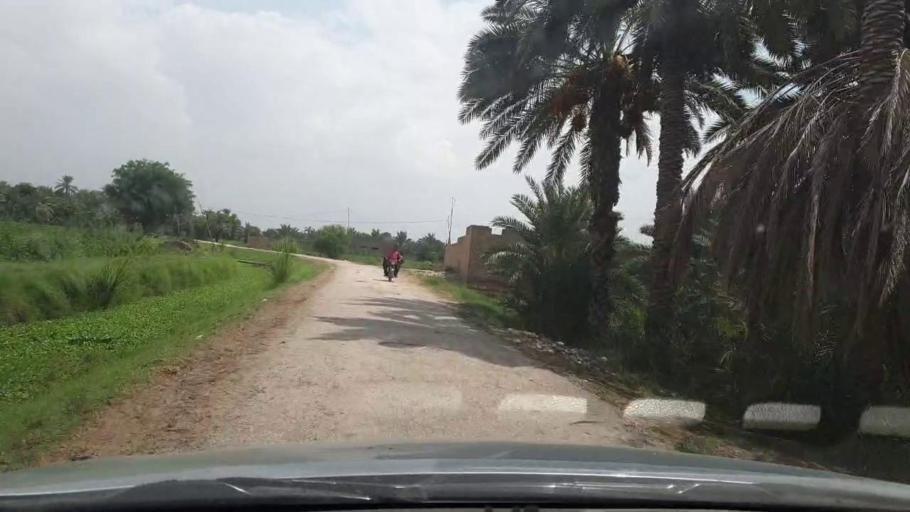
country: PK
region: Sindh
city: Kot Diji
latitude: 27.4165
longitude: 68.7586
